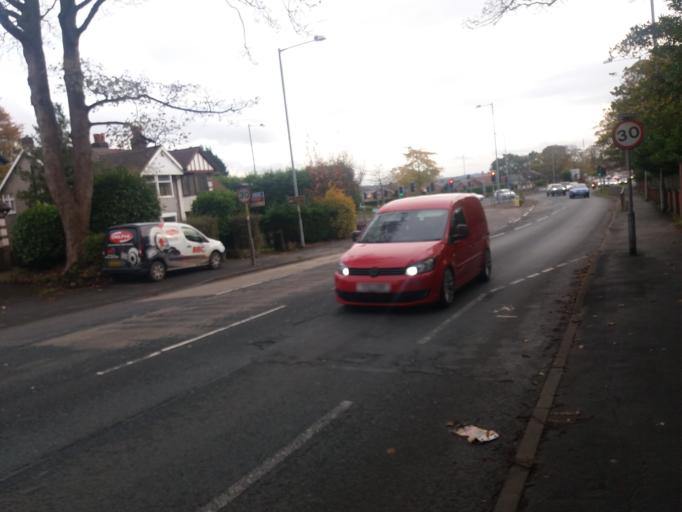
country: GB
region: England
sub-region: Lancashire
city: Chorley
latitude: 53.6693
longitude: -2.6323
